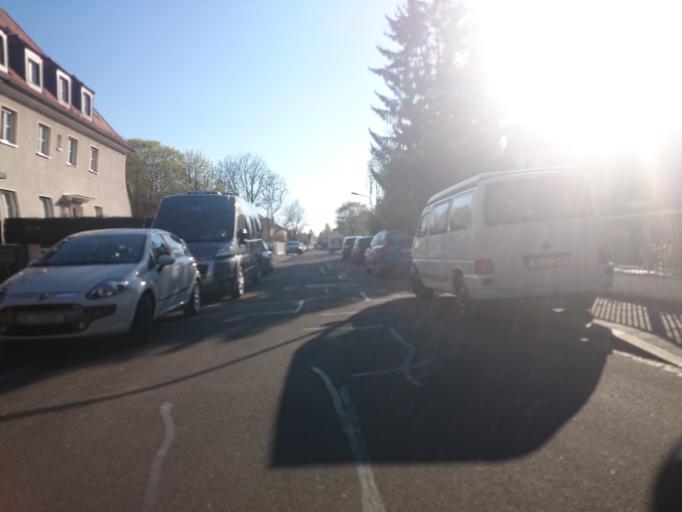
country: DE
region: Bavaria
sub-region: Regierungsbezirk Mittelfranken
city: Nuernberg
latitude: 49.4569
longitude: 11.1313
